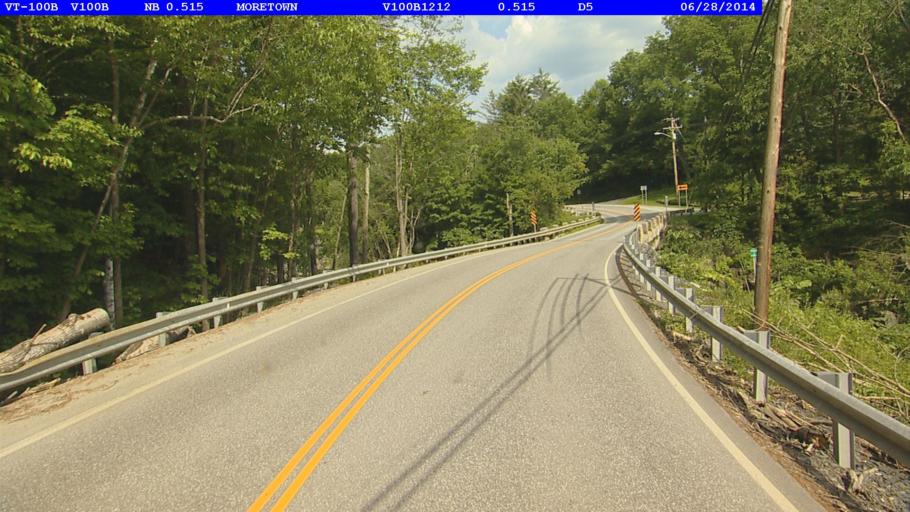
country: US
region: Vermont
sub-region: Washington County
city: Waterbury
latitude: 44.2456
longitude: -72.7701
